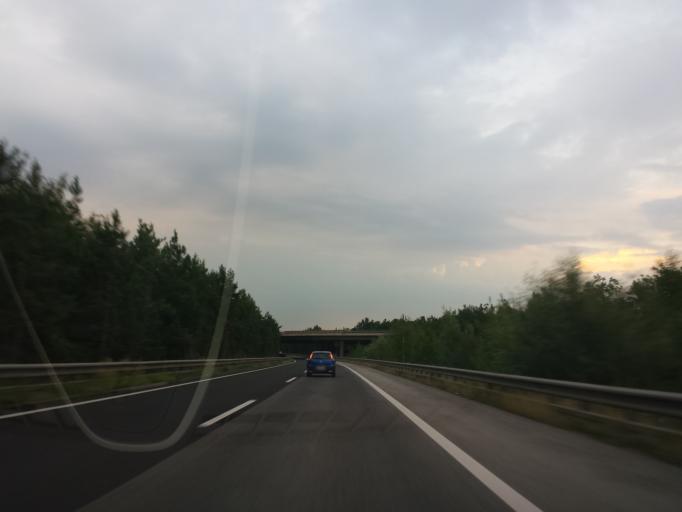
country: AT
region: Lower Austria
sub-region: Politischer Bezirk Neunkirchen
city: Breitenau
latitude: 47.7137
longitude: 16.1289
